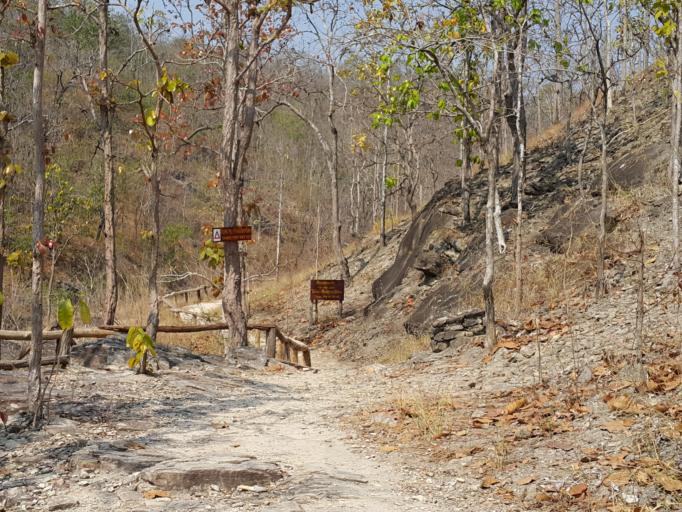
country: TH
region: Chiang Mai
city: Hang Dong
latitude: 18.7229
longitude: 98.8207
